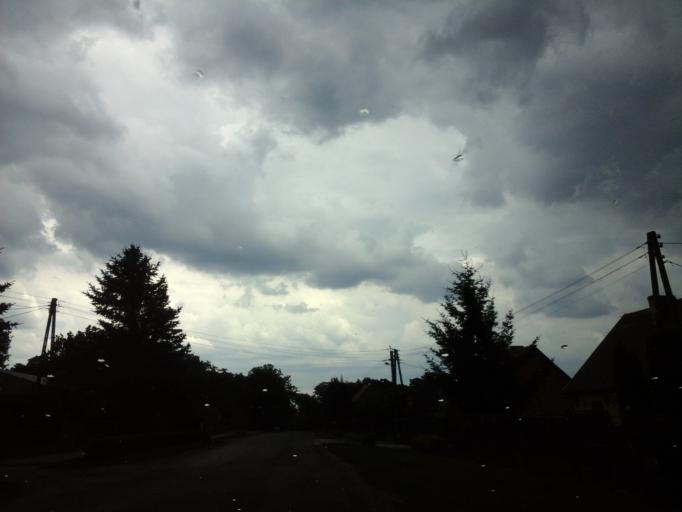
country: PL
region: West Pomeranian Voivodeship
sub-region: Powiat choszczenski
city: Drawno
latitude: 53.2092
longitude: 15.8021
